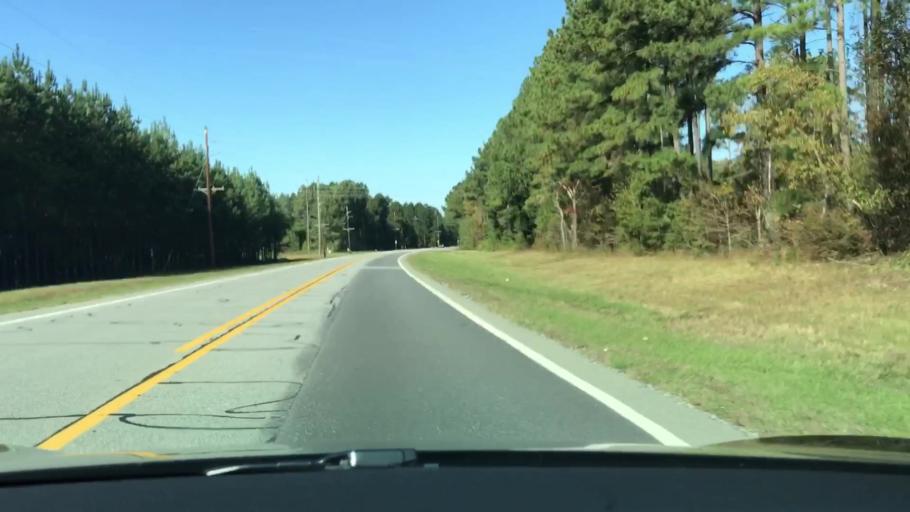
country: US
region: Georgia
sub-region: Warren County
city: Warrenton
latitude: 33.3898
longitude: -82.6440
